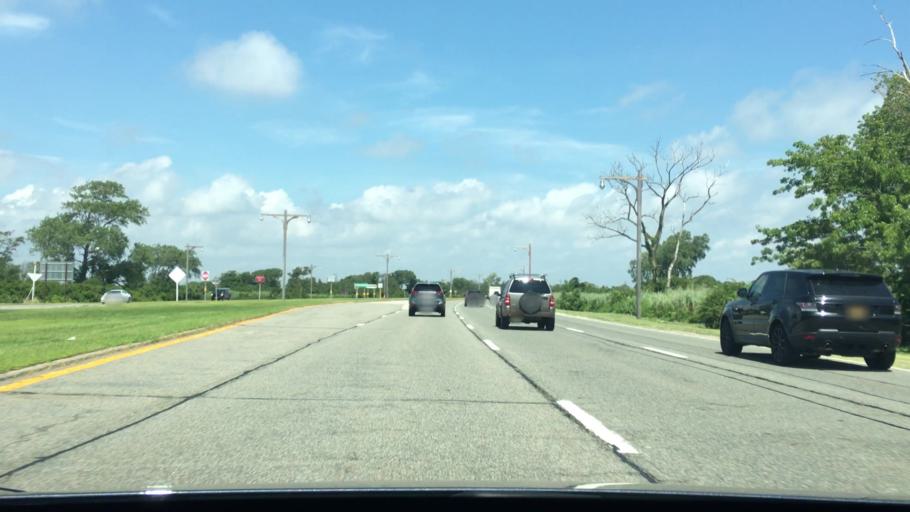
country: US
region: New York
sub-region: Nassau County
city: Point Lookout
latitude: 40.6199
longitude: -73.5597
